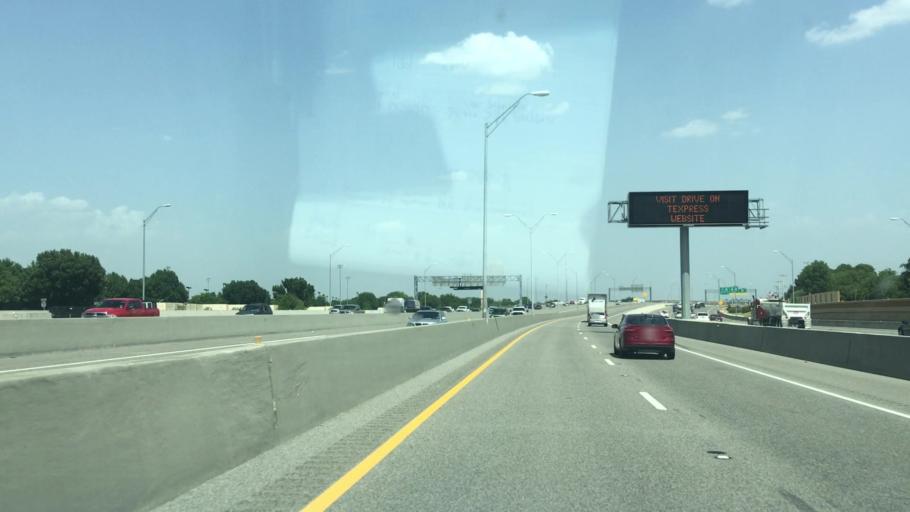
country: US
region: Texas
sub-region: Tarrant County
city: North Richland Hills
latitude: 32.8399
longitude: -97.2326
